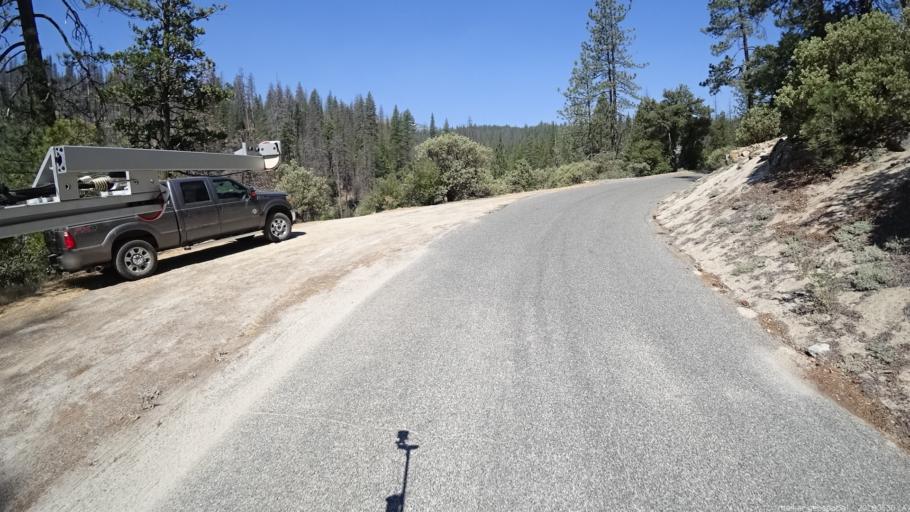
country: US
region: California
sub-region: Madera County
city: Oakhurst
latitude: 37.3609
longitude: -119.3503
